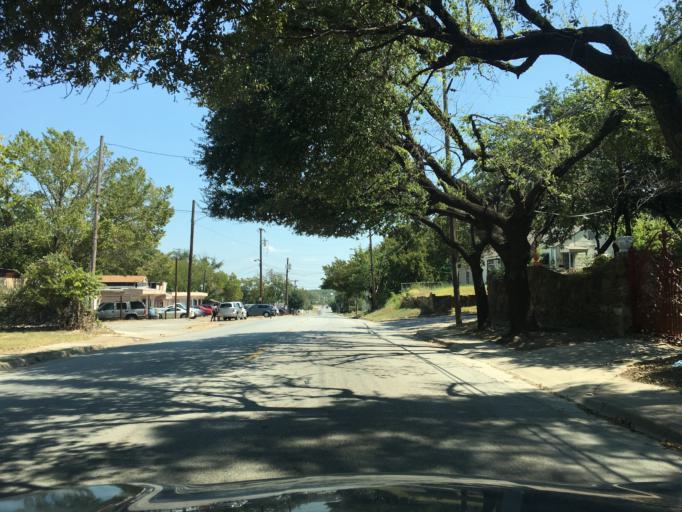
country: US
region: Texas
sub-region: Dallas County
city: Dallas
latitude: 32.7463
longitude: -96.7929
